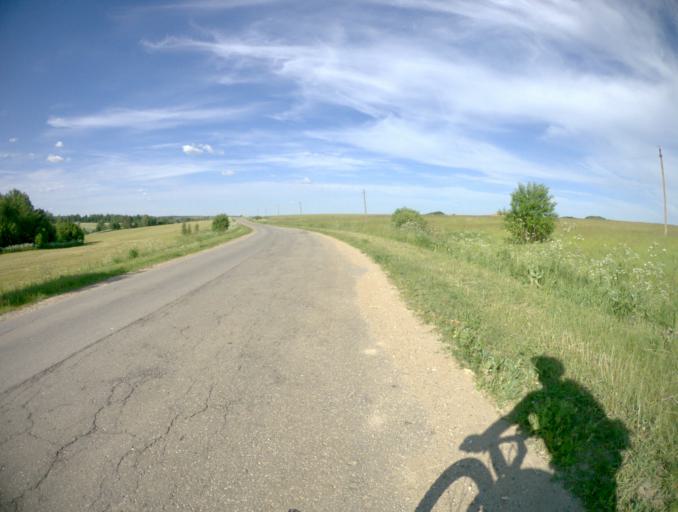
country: RU
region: Vladimir
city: Stavrovo
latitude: 56.1562
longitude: 40.1226
